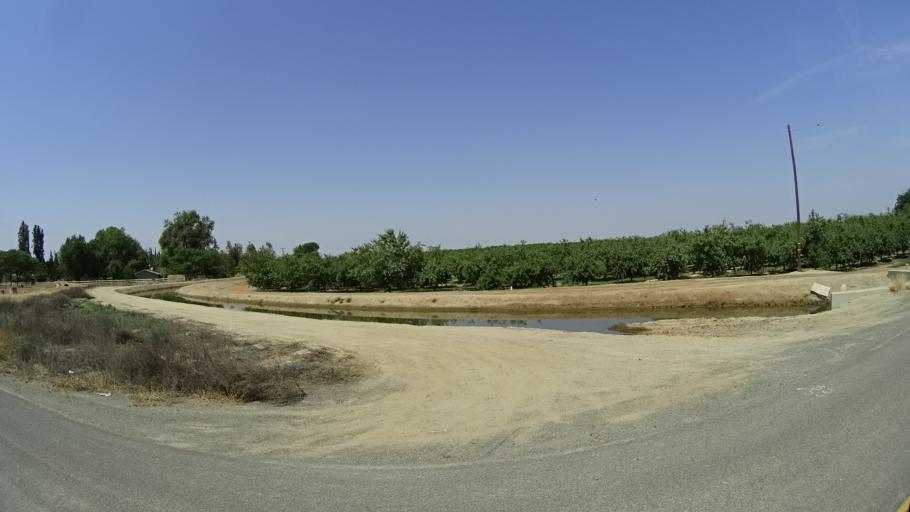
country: US
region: California
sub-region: Kings County
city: Lemoore
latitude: 36.3030
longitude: -119.7447
